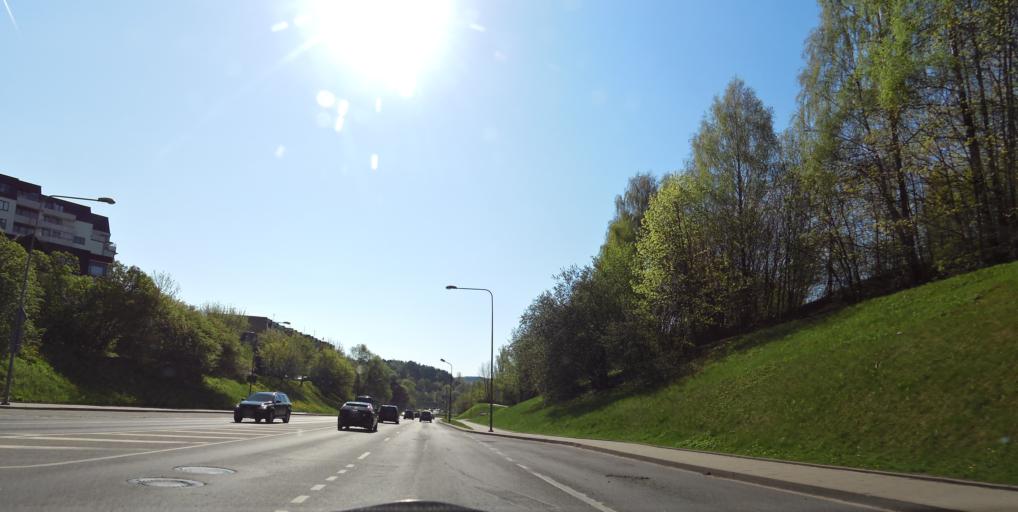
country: LT
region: Vilnius County
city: Rasos
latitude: 54.6848
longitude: 25.3091
